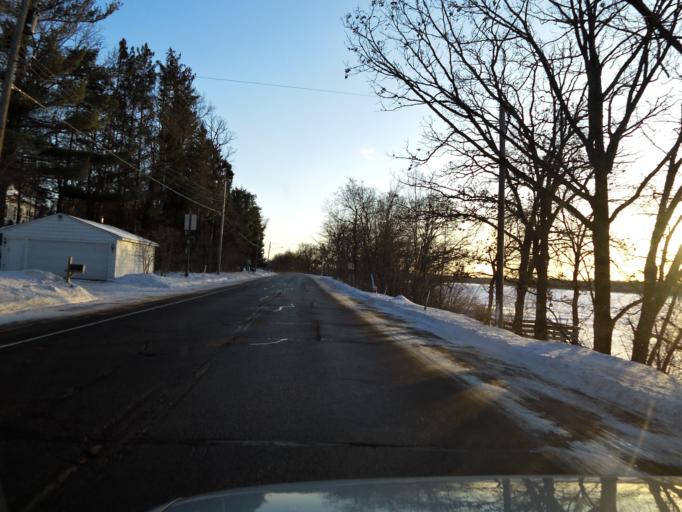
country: US
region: Minnesota
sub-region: Washington County
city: Lake Elmo
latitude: 44.9898
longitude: -92.8804
